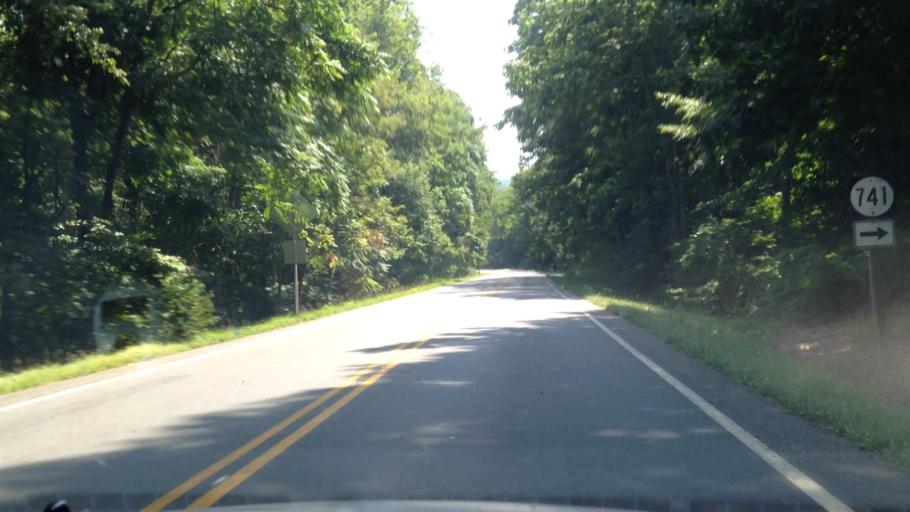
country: US
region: Virginia
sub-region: Patrick County
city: Stuart
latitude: 36.5896
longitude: -80.3266
